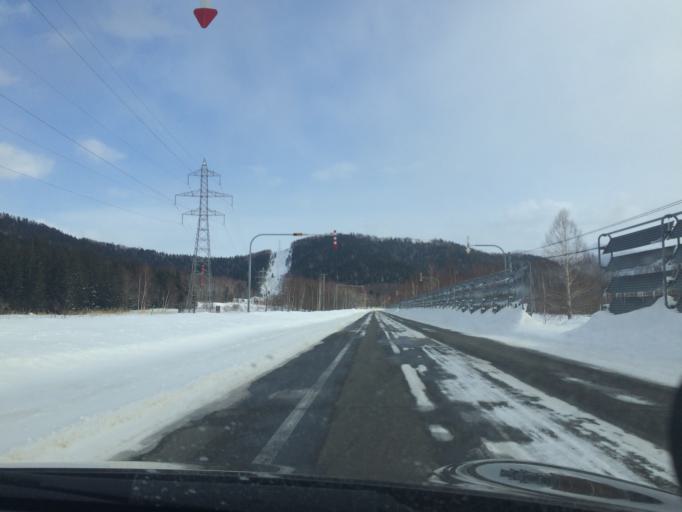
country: JP
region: Hokkaido
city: Shimo-furano
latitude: 43.0544
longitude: 142.6367
